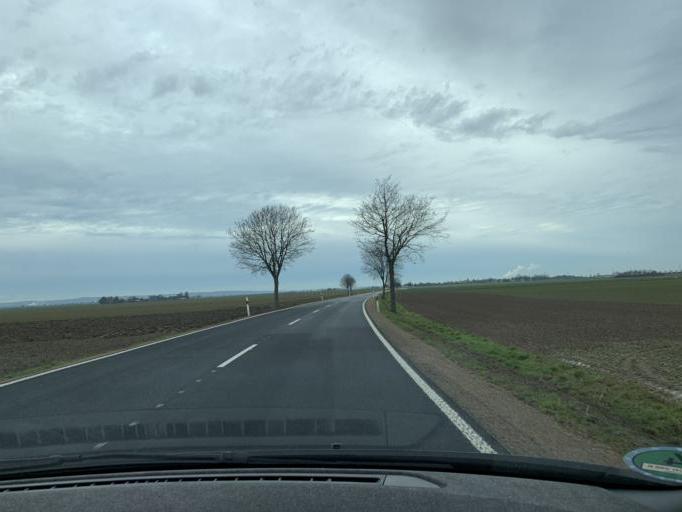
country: DE
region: North Rhine-Westphalia
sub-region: Regierungsbezirk Koln
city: Norvenich
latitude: 50.7897
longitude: 6.6034
